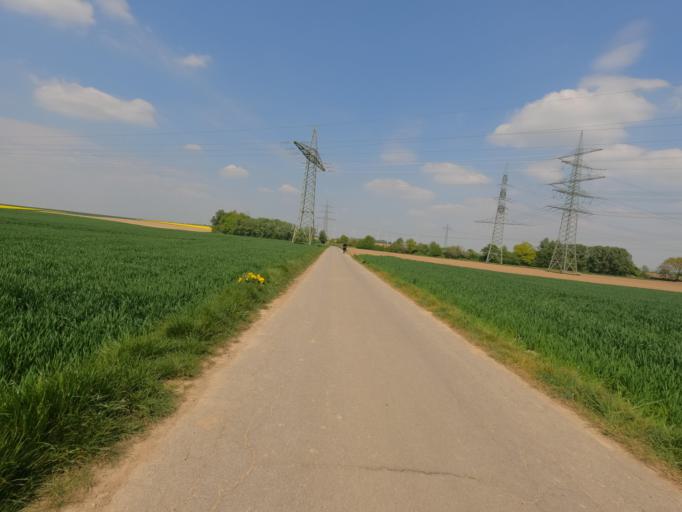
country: DE
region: North Rhine-Westphalia
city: Baesweiler
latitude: 50.9424
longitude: 6.2117
